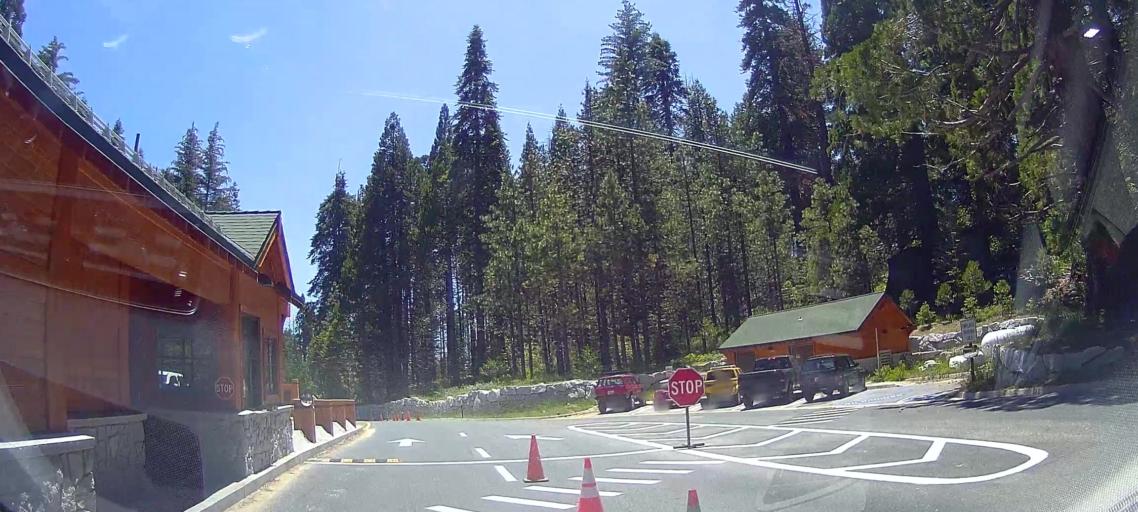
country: US
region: California
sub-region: Fresno County
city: Squaw Valley
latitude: 36.7162
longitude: -118.9643
